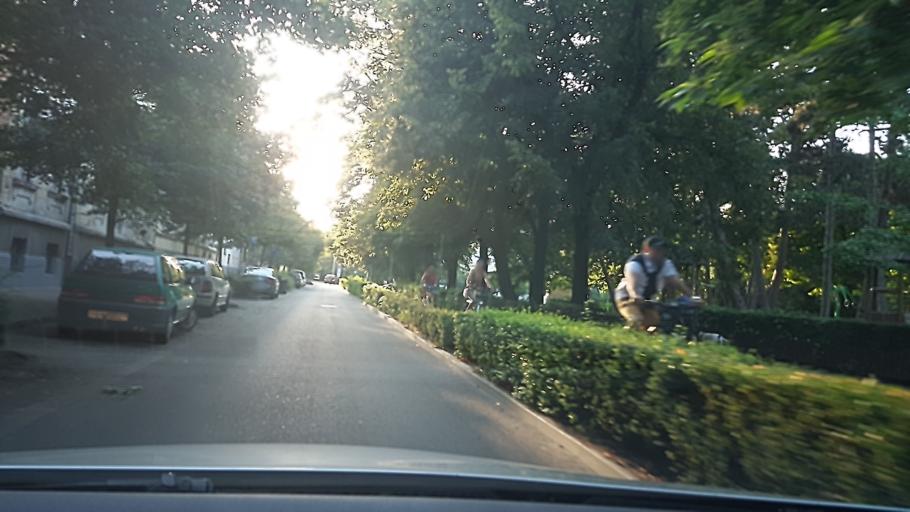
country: HU
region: Gyor-Moson-Sopron
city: Sopron
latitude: 47.6815
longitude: 16.5838
